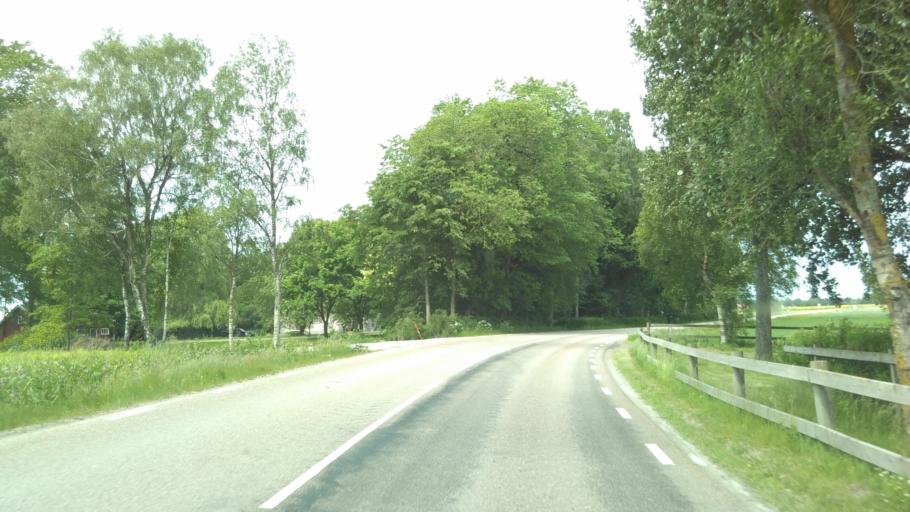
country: SE
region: Vaestra Goetaland
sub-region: Lidkopings Kommun
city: Lidkoping
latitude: 58.4664
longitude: 13.1459
